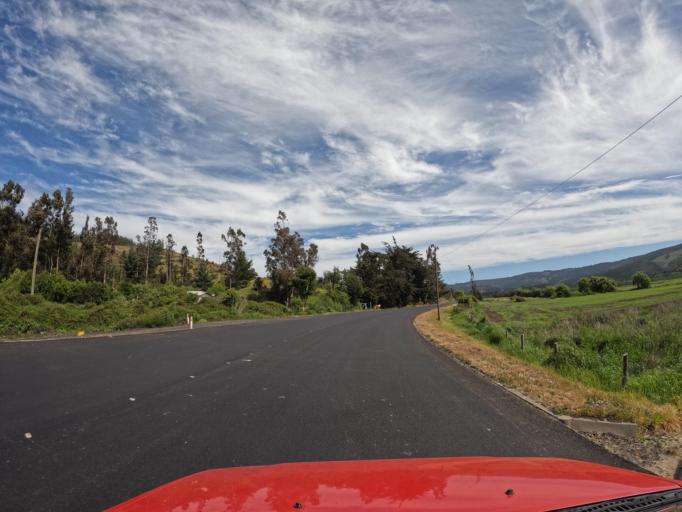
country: CL
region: Maule
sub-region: Provincia de Talca
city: Constitucion
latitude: -35.0680
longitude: -72.0377
